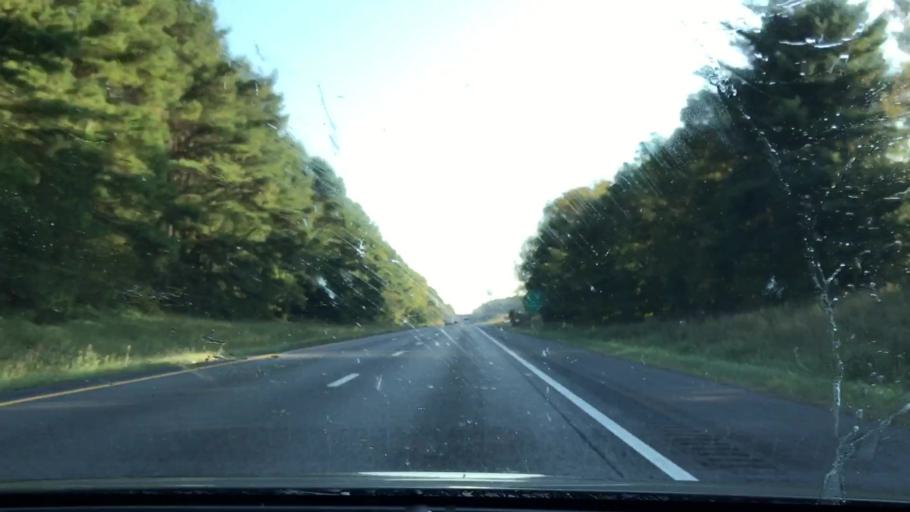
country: US
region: Tennessee
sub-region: Sumner County
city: Portland
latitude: 36.5872
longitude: -86.6054
